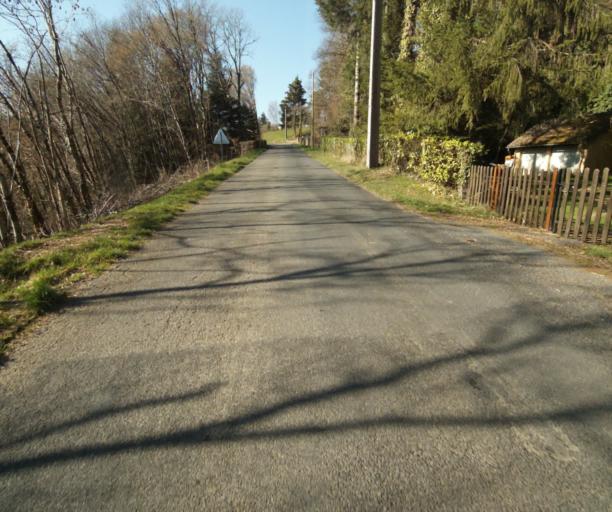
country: FR
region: Limousin
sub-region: Departement de la Correze
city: Tulle
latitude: 45.2905
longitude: 1.7250
